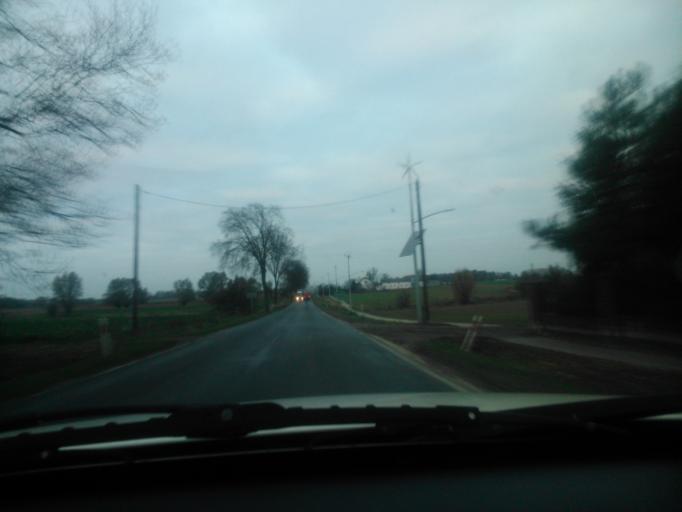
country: PL
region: Kujawsko-Pomorskie
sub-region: Powiat golubsko-dobrzynski
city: Kowalewo Pomorskie
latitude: 53.1565
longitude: 18.9362
